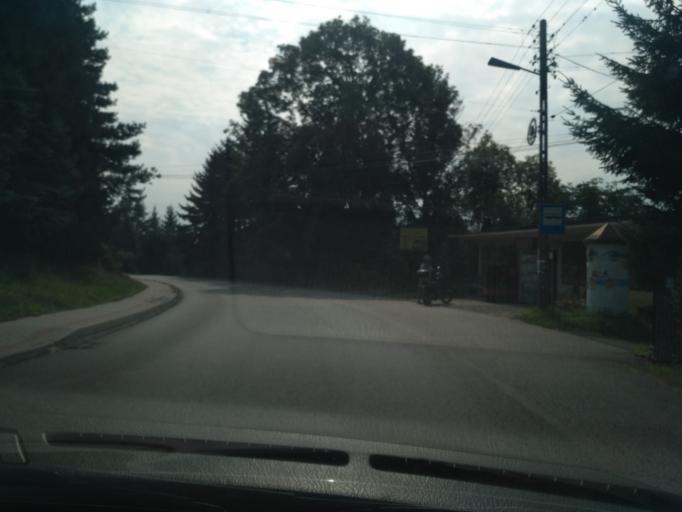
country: PL
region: Subcarpathian Voivodeship
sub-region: Powiat rzeszowski
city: Kielanowka
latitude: 50.0018
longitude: 21.9168
